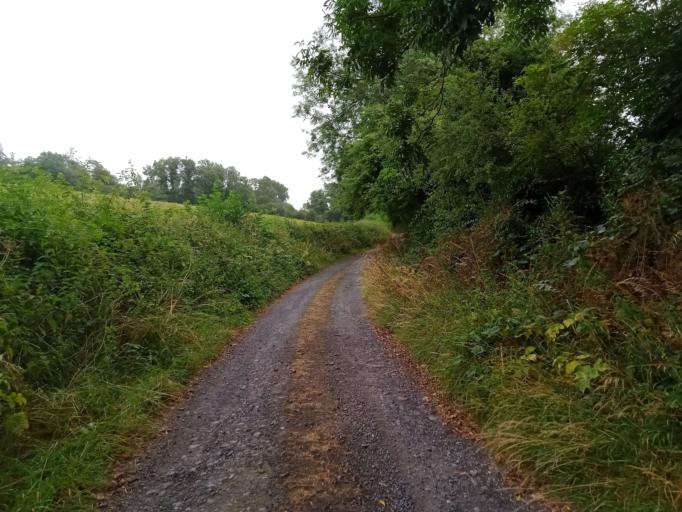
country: IE
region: Leinster
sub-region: Kilkenny
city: Ballyragget
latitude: 52.8118
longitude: -7.4311
